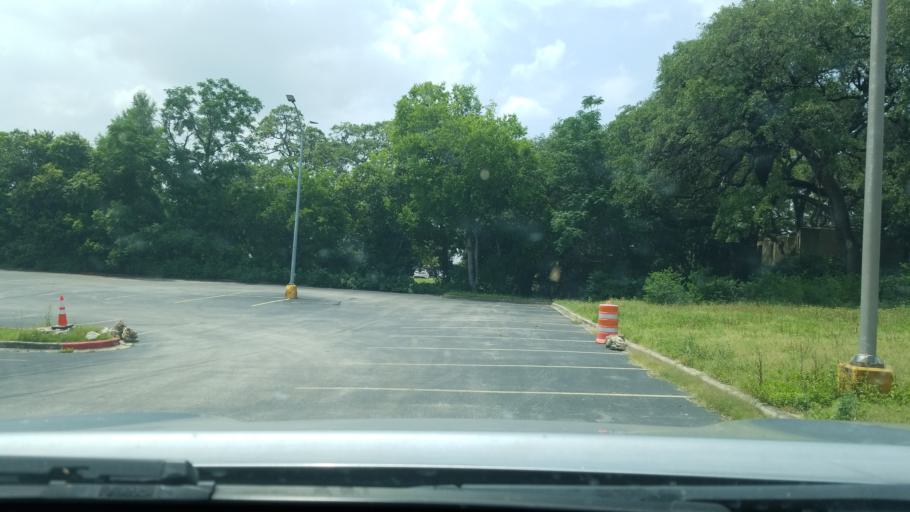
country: US
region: Texas
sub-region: Comal County
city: New Braunfels
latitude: 29.6998
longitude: -98.0957
